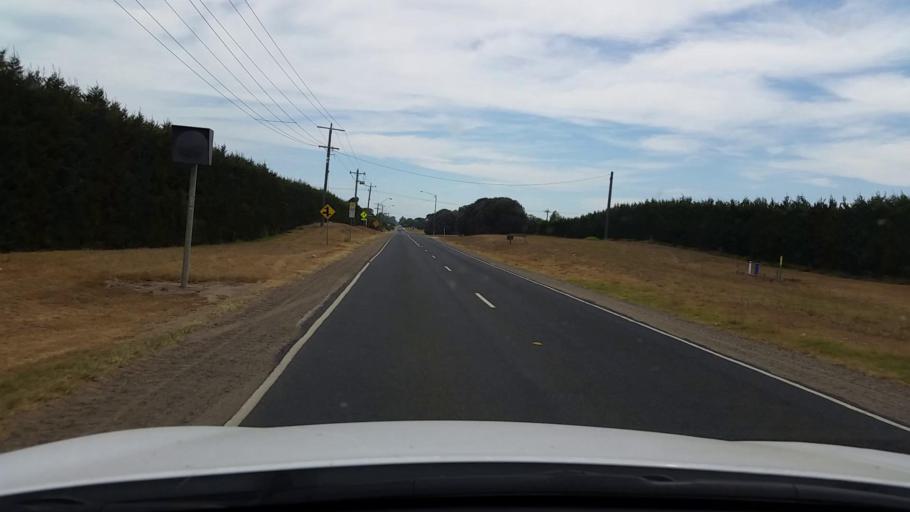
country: AU
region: Victoria
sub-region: Mornington Peninsula
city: Rosebud West
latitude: -38.4145
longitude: 144.8874
